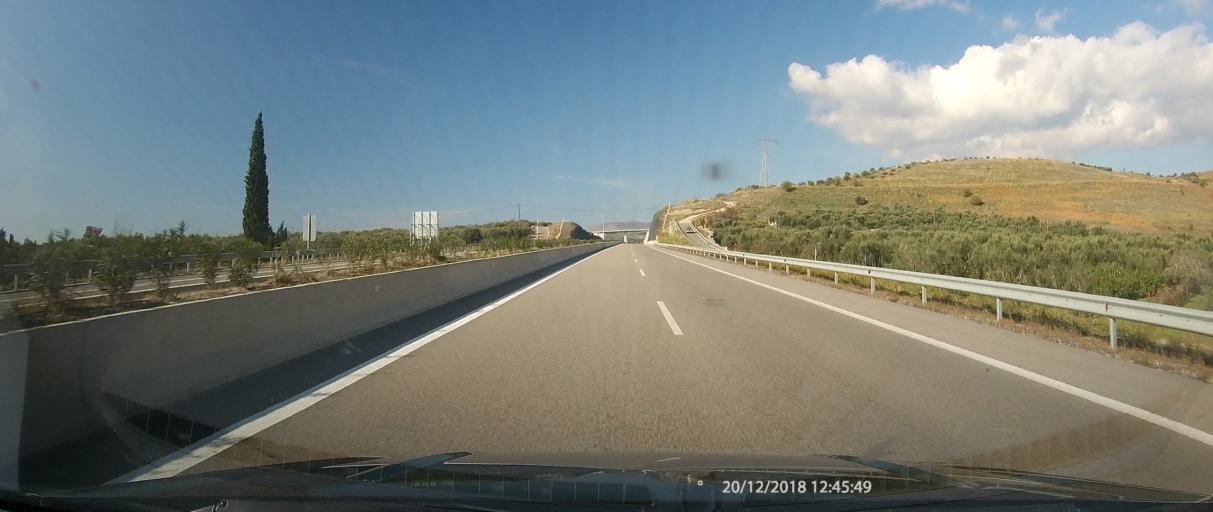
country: GR
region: West Greece
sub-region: Nomos Aitolias kai Akarnanias
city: Mesolongi
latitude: 38.3849
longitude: 21.4871
